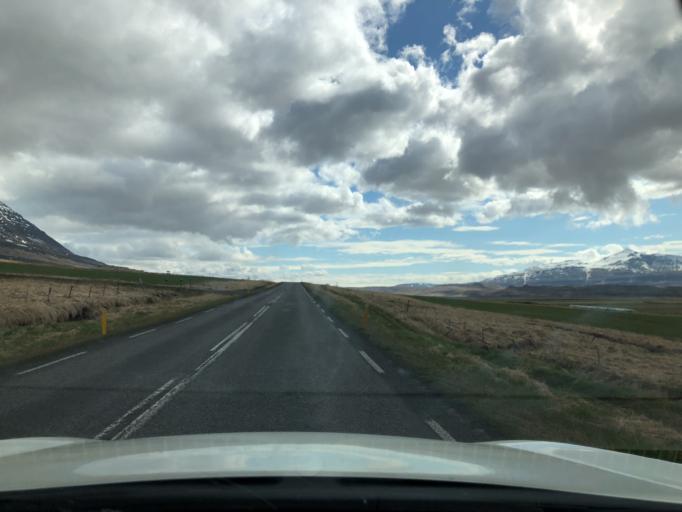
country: IS
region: Northwest
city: Saudarkrokur
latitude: 65.5190
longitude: -19.3038
